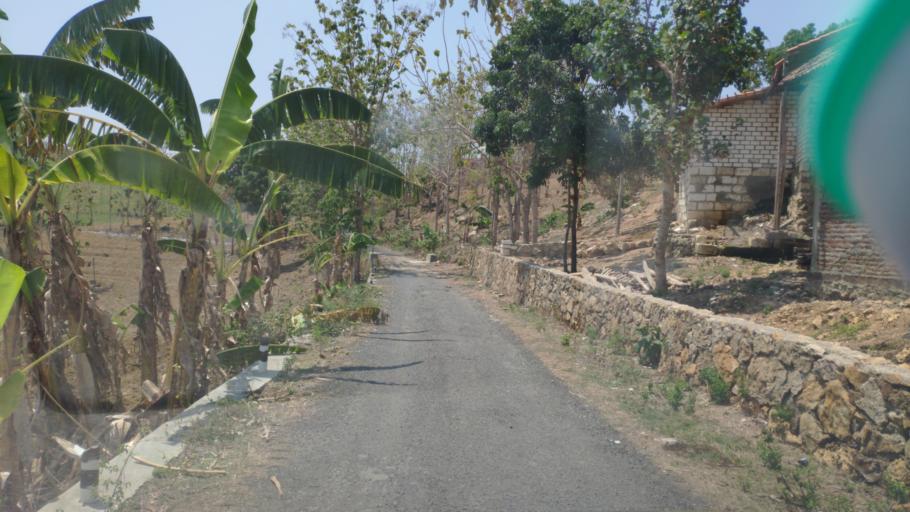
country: ID
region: Central Java
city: Ngapus
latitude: -6.9196
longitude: 111.2023
